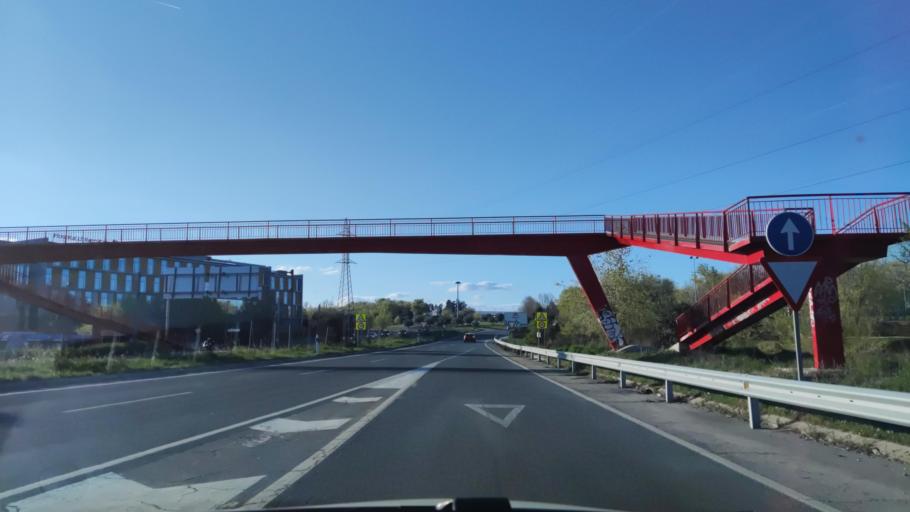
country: ES
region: Madrid
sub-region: Provincia de Madrid
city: Latina
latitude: 40.4020
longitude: -3.7804
